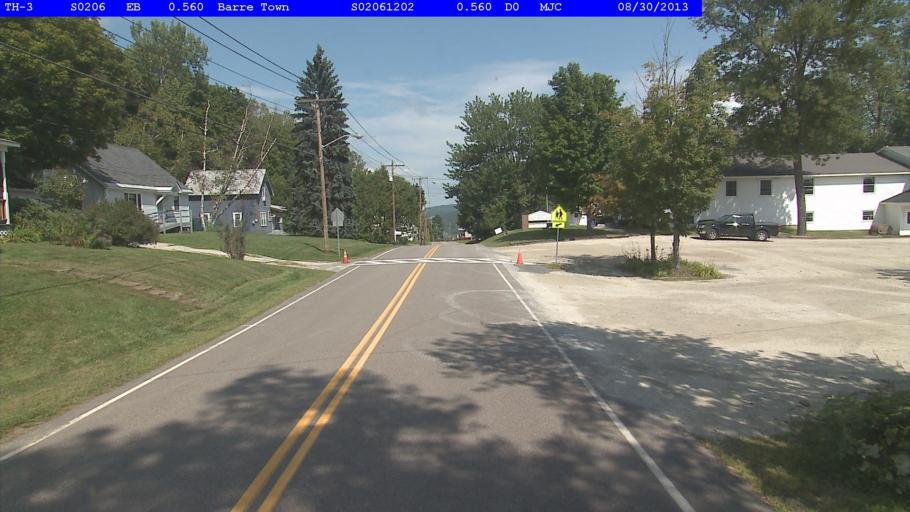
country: US
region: Vermont
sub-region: Washington County
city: South Barre
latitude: 44.1528
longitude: -72.4748
